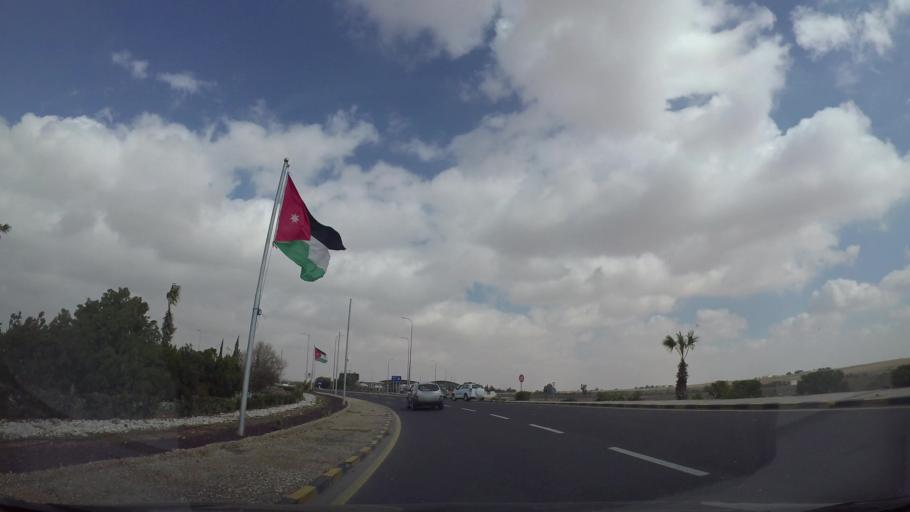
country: JO
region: Amman
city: Al Jizah
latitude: 31.7201
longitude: 35.9682
